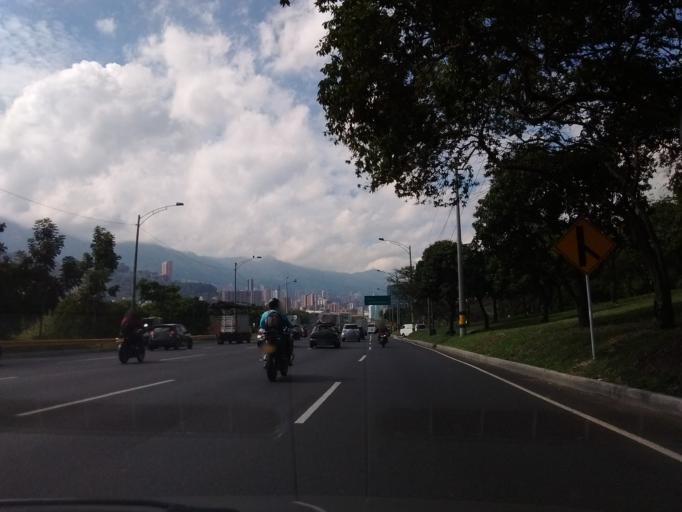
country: CO
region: Antioquia
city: Medellin
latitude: 6.2362
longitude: -75.5767
